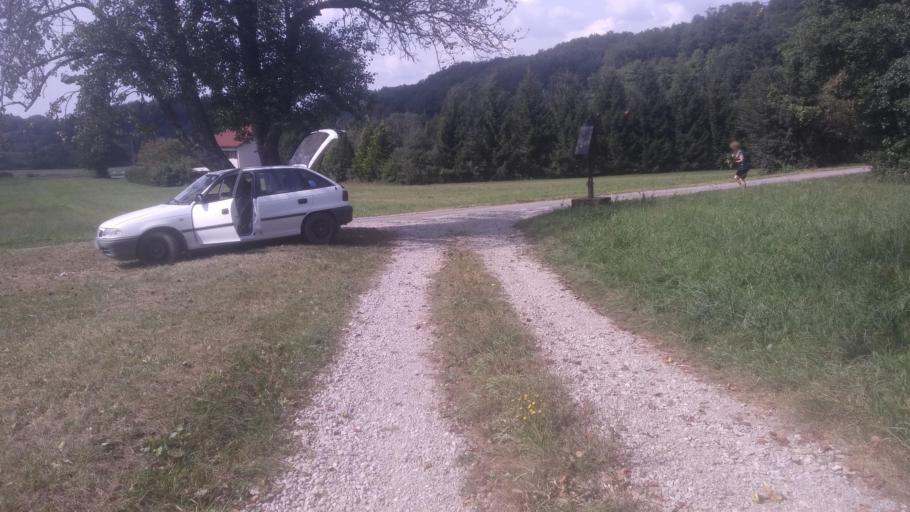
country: SI
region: Pivka
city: Pivka
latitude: 45.5967
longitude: 14.2061
